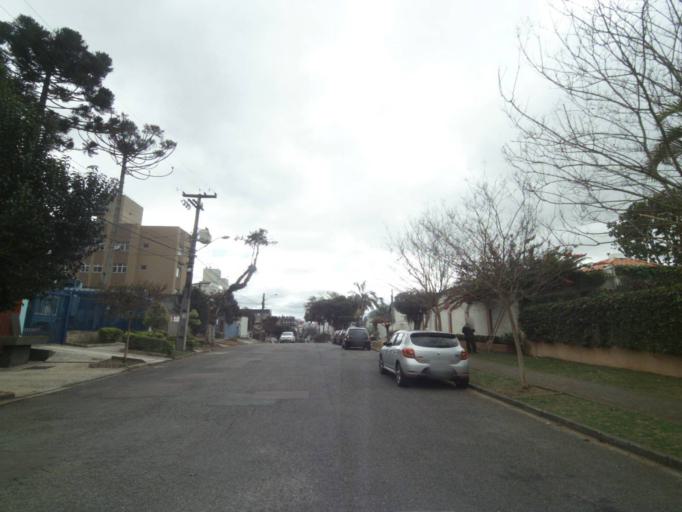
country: BR
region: Parana
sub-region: Curitiba
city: Curitiba
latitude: -25.4678
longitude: -49.2884
